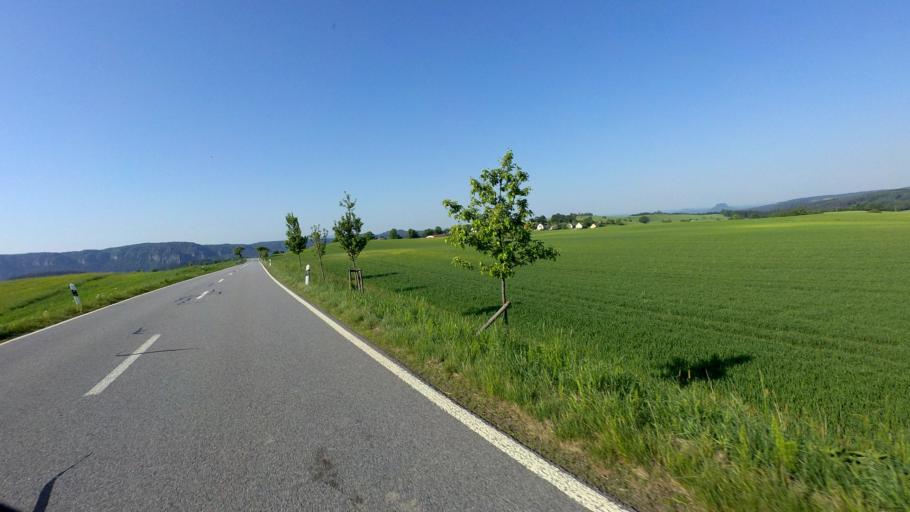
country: DE
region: Saxony
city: Sebnitz
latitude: 50.9510
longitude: 14.2461
